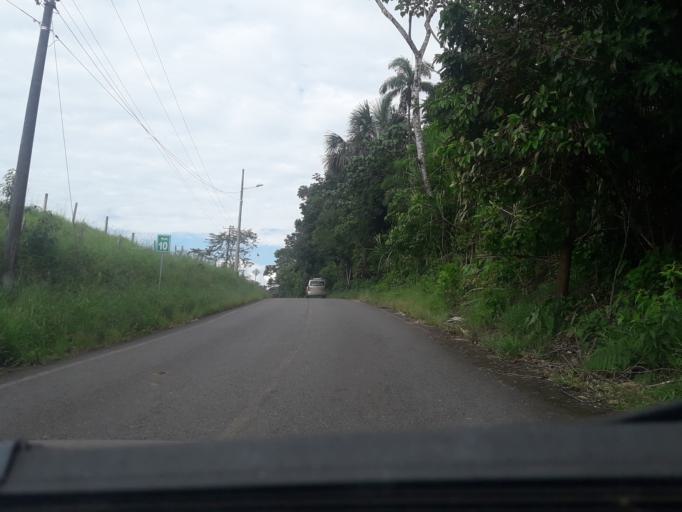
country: EC
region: Napo
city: Tena
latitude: -1.0350
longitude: -77.8904
